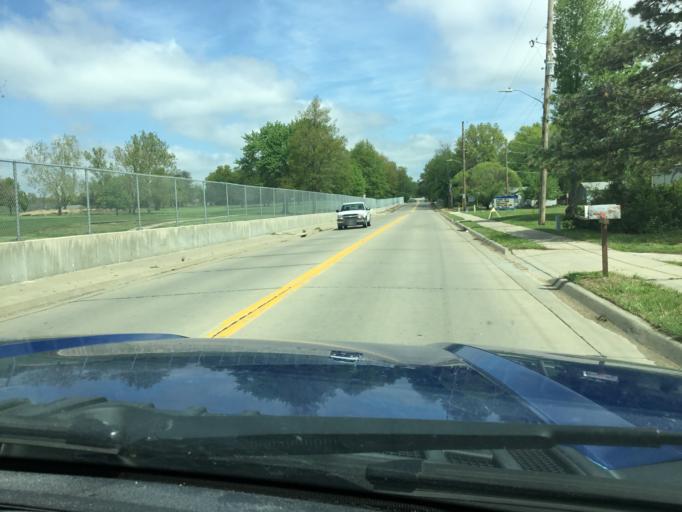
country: US
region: Kansas
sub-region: Shawnee County
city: Topeka
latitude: 39.0088
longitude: -95.6609
